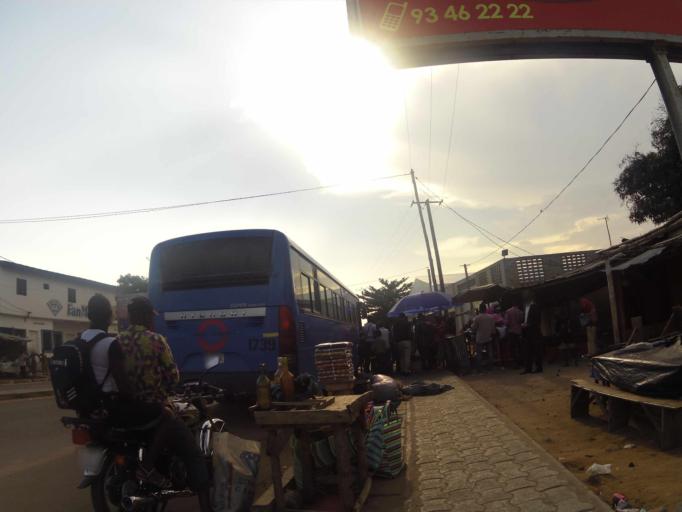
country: TG
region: Maritime
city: Aneho
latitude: 6.2408
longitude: 1.6253
